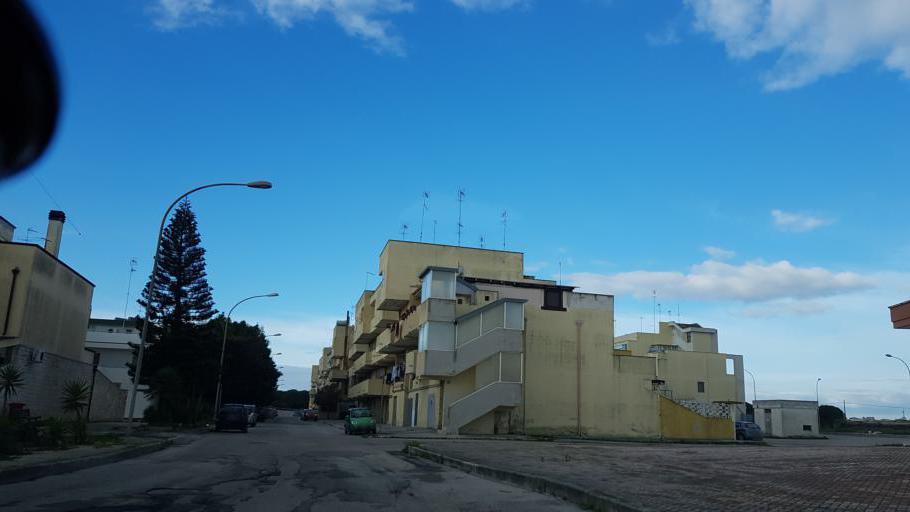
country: IT
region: Apulia
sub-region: Provincia di Brindisi
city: Brindisi
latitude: 40.6275
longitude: 17.9565
